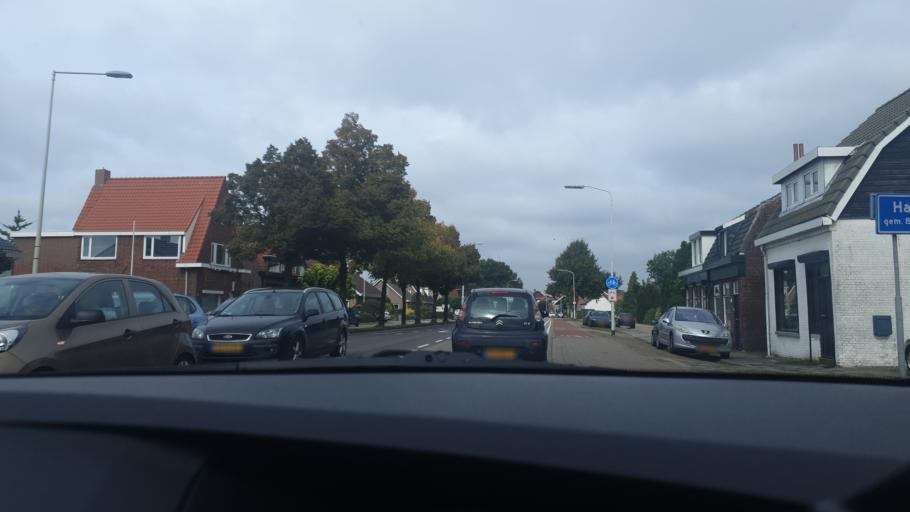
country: NL
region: North Brabant
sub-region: Gemeente Bergen op Zoom
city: Halsteren
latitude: 51.5118
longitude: 4.2788
